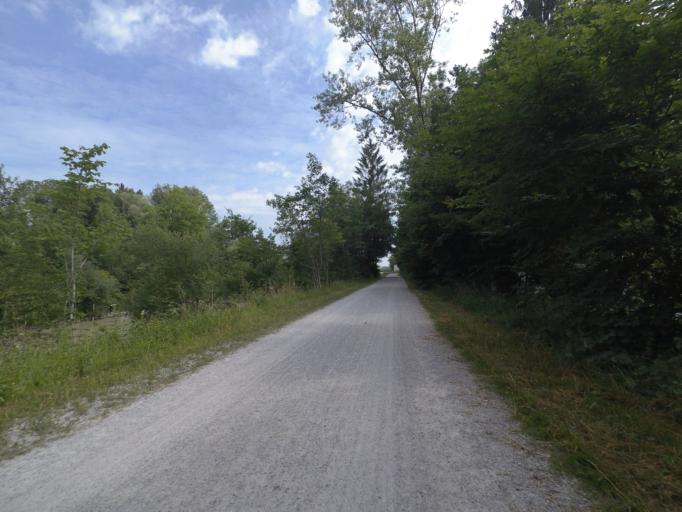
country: DE
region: Bavaria
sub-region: Upper Bavaria
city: Ainring
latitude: 47.8097
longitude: 12.9729
